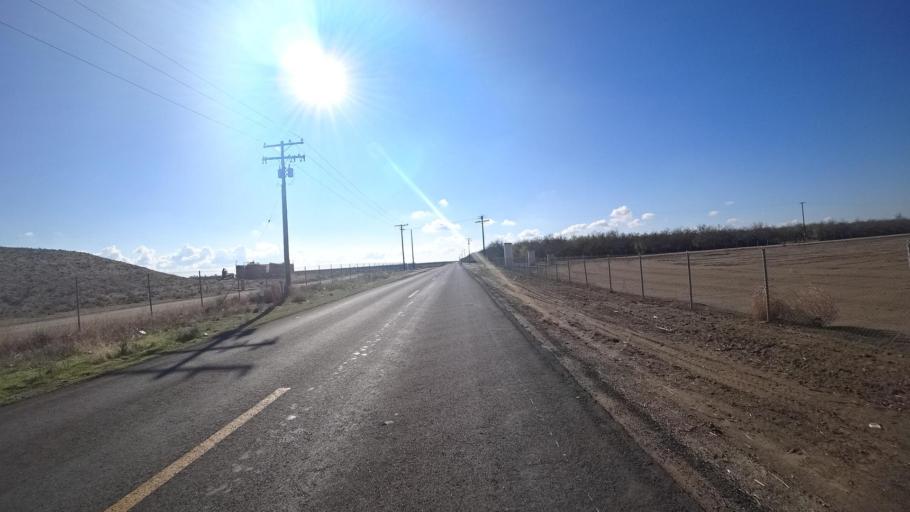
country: US
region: California
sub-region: Kern County
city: Delano
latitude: 35.7403
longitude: -119.2584
